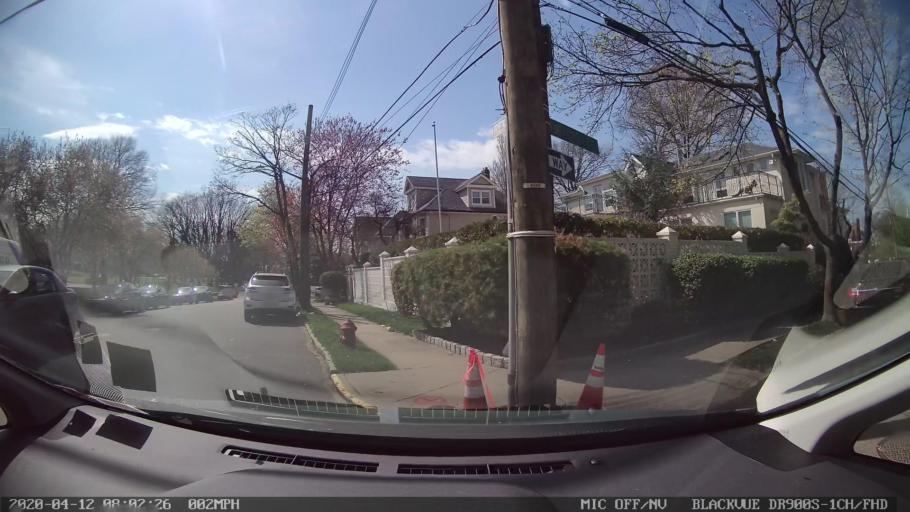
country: US
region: New Jersey
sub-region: Hudson County
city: Bayonne
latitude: 40.6287
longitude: -74.0991
